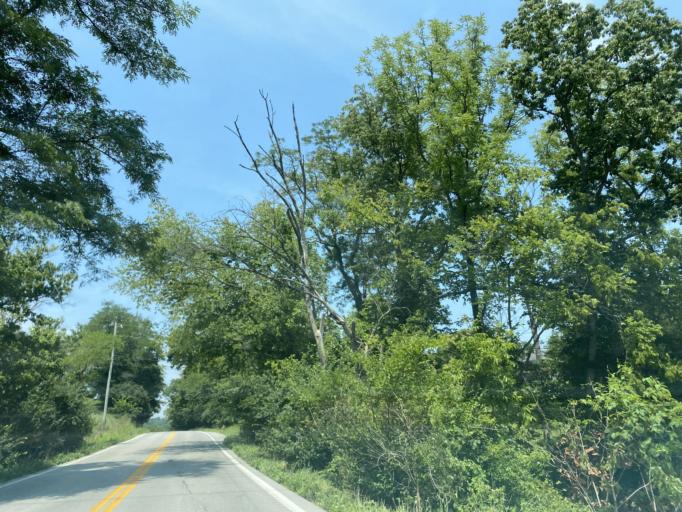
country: US
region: Kentucky
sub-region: Campbell County
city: Claryville
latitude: 38.9057
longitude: -84.4467
